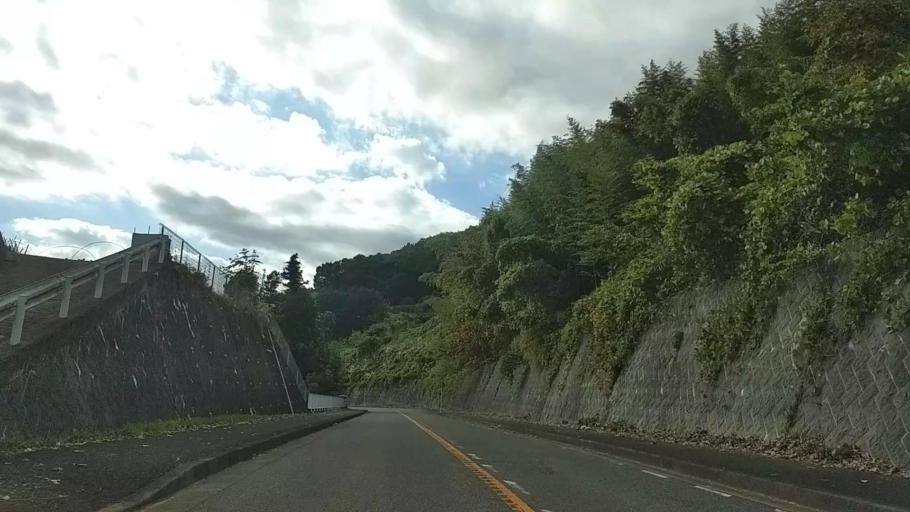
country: JP
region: Kanagawa
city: Hadano
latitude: 35.3589
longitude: 139.1780
